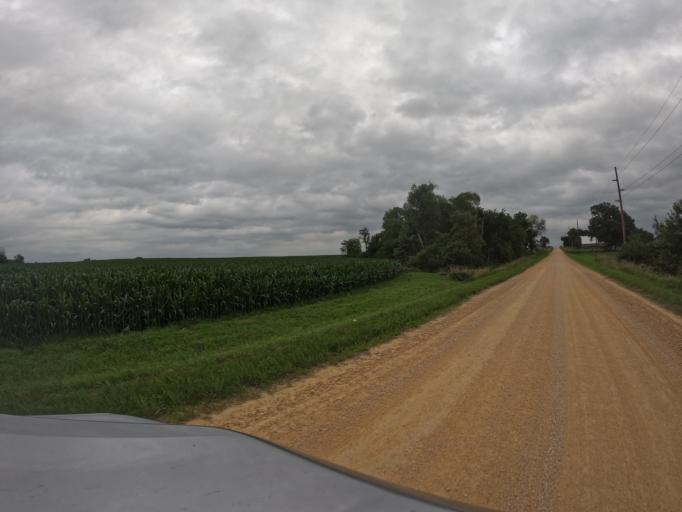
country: US
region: Iowa
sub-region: Clinton County
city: De Witt
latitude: 41.7863
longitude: -90.4681
